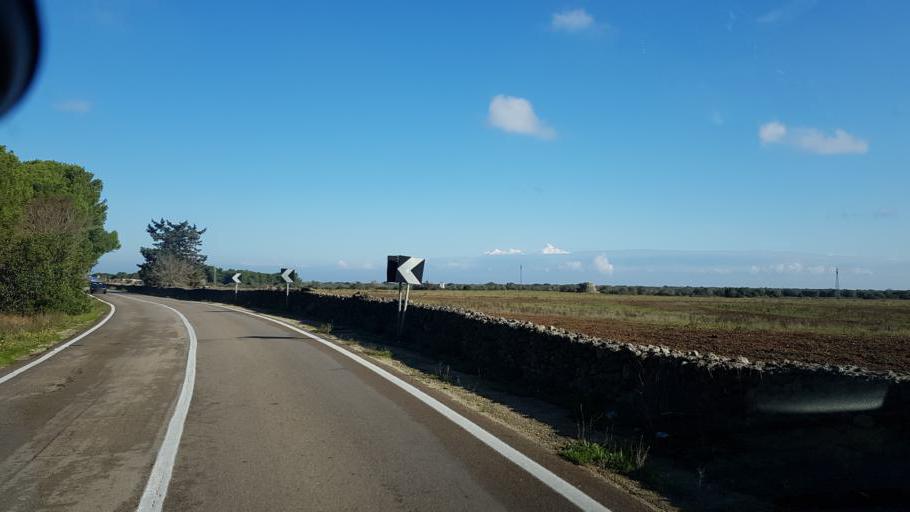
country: IT
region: Apulia
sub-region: Provincia di Lecce
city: Trepuzzi
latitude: 40.4531
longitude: 18.1117
